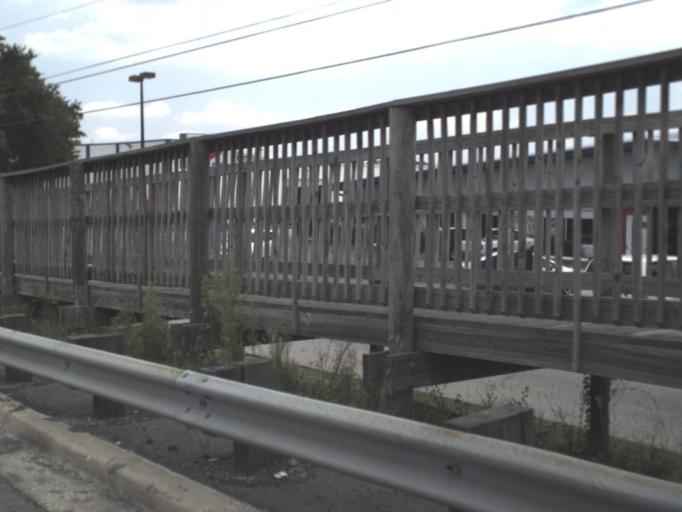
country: US
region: Florida
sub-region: Pinellas County
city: Lealman
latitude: 27.8117
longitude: -82.6794
